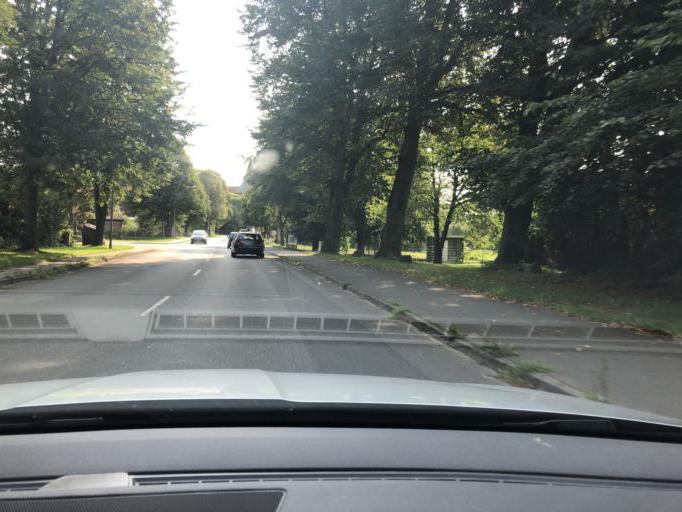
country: DE
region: Schleswig-Holstein
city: Gross Gronau
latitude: 53.7997
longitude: 10.7515
